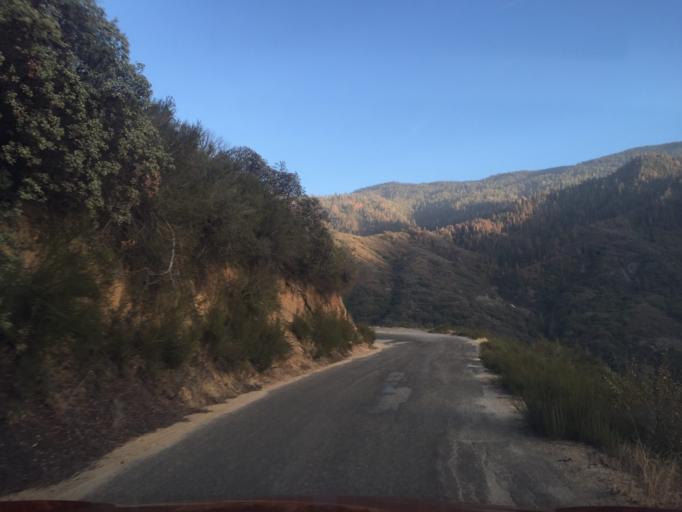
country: US
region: California
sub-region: Tulare County
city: Three Rivers
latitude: 36.4305
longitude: -118.7507
